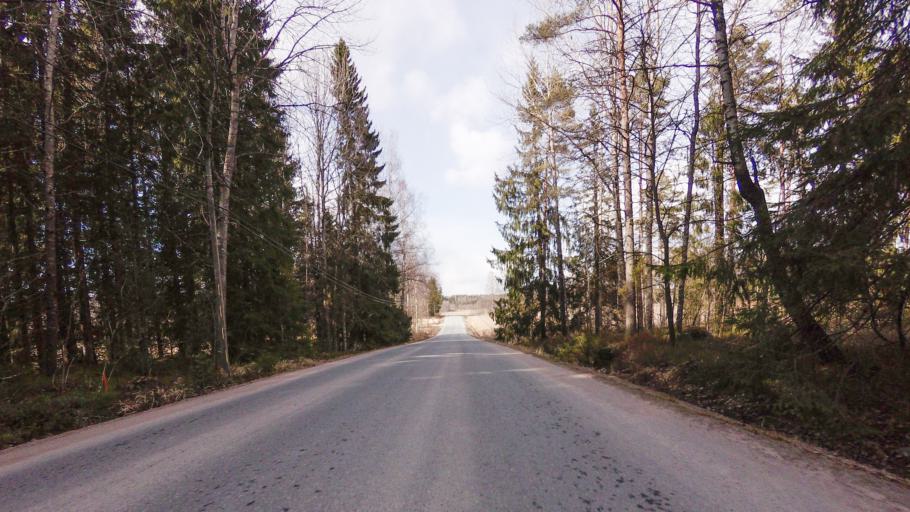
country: FI
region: Varsinais-Suomi
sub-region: Salo
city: Suomusjaervi
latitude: 60.3340
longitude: 23.7039
